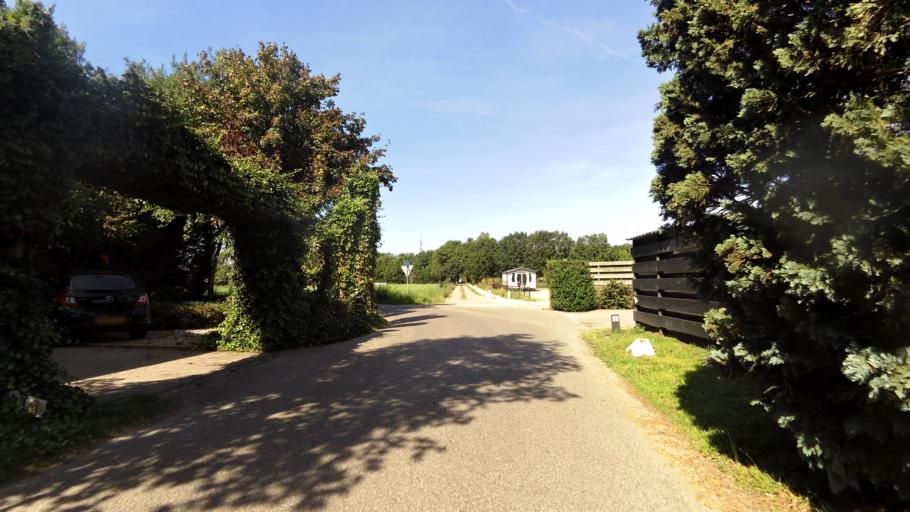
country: NL
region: Gelderland
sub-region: Gemeente Ede
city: Harskamp
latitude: 52.1375
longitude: 5.7532
